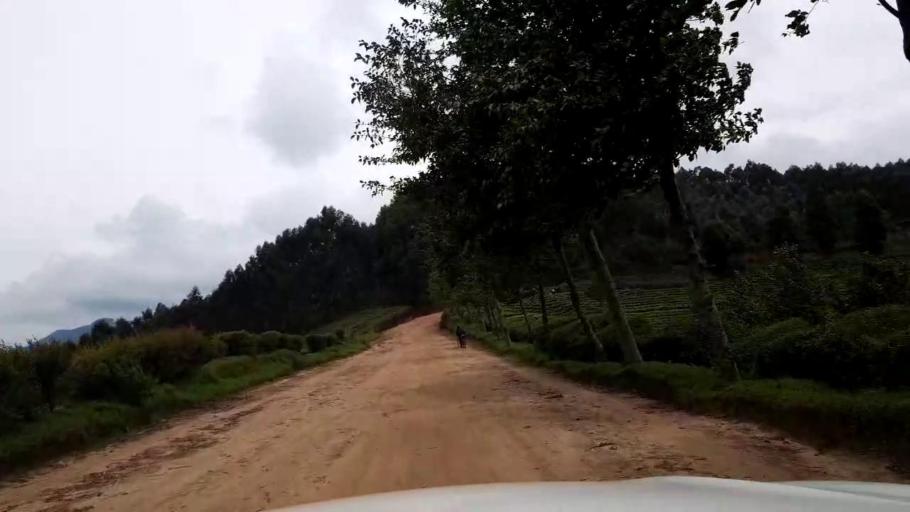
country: RW
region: Western Province
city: Kibuye
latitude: -1.9524
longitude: 29.4081
